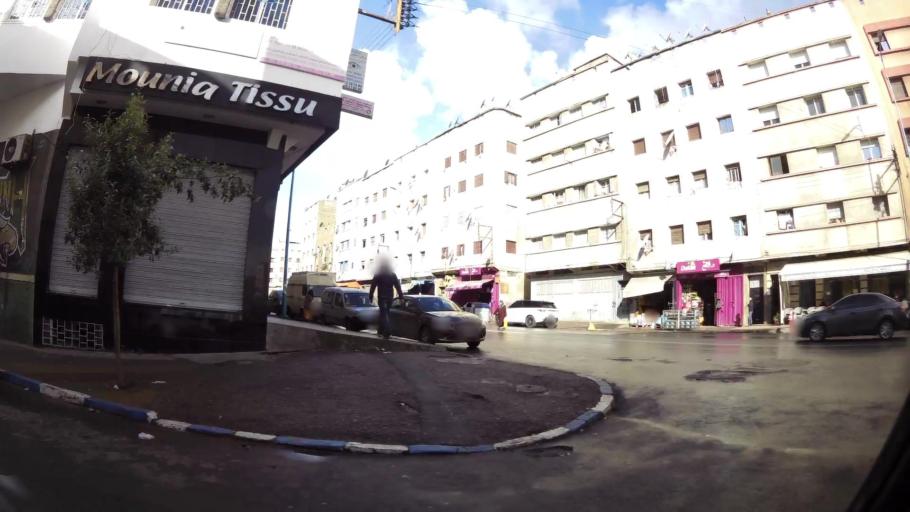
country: MA
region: Grand Casablanca
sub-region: Casablanca
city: Casablanca
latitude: 33.5656
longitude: -7.5866
